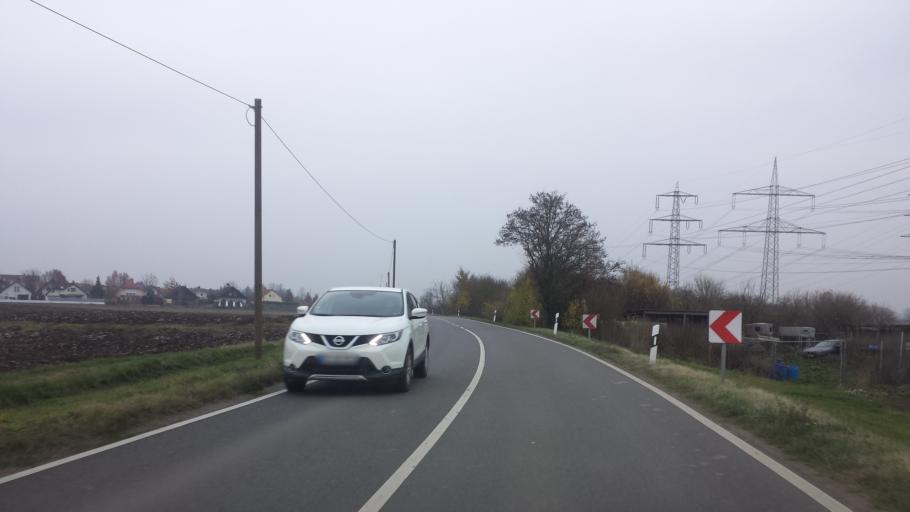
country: DE
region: Rheinland-Pfalz
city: Worms
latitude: 49.6610
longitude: 8.3940
